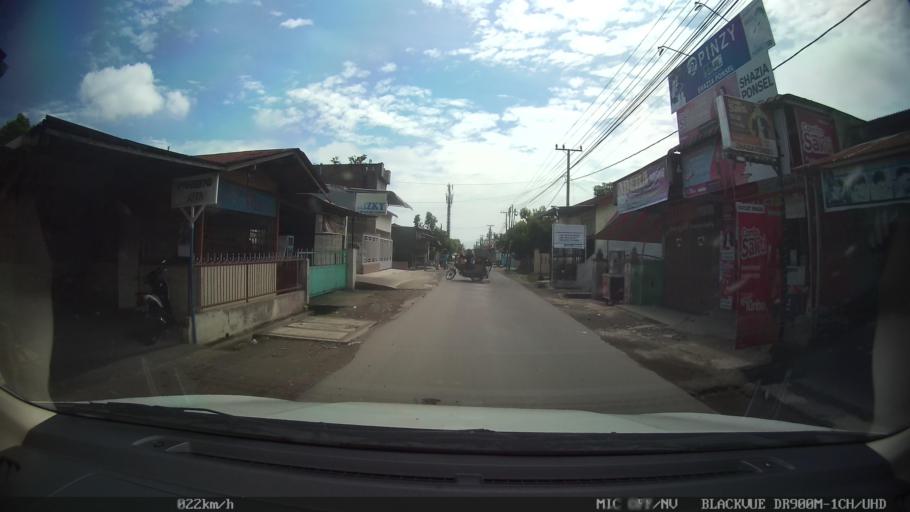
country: ID
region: North Sumatra
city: Medan
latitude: 3.5910
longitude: 98.7428
